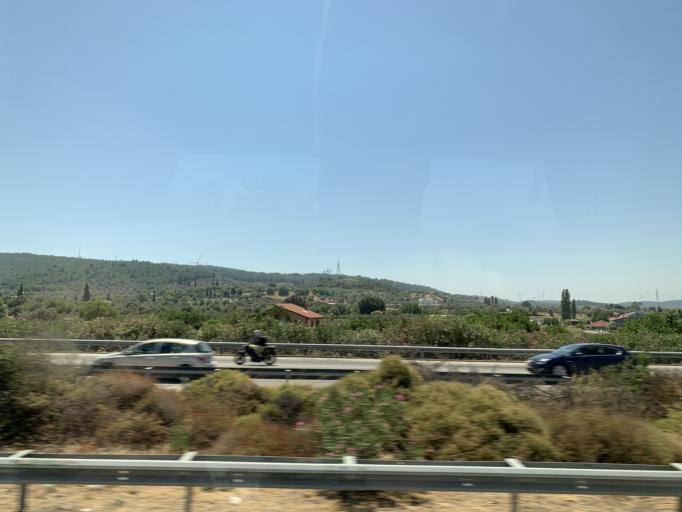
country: TR
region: Izmir
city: Urla
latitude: 38.3037
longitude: 26.7537
